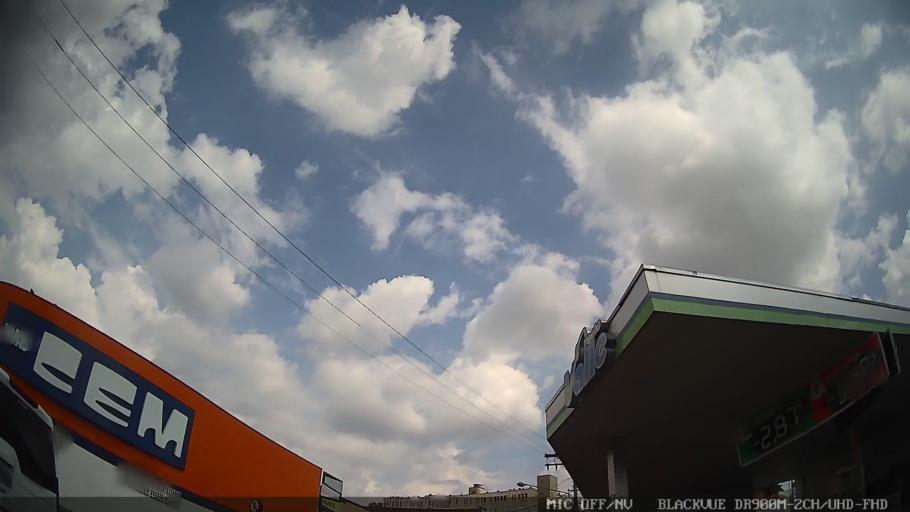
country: BR
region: Sao Paulo
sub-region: Braganca Paulista
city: Braganca Paulista
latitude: -22.9499
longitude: -46.5446
